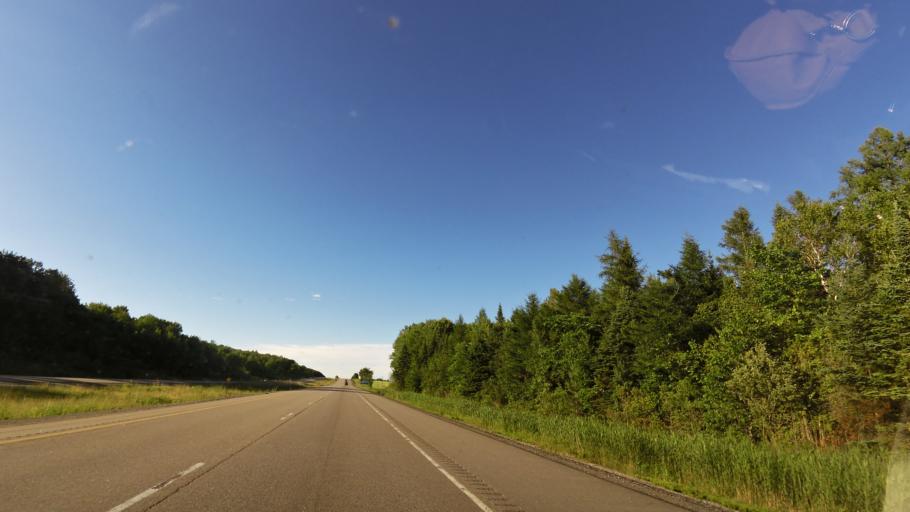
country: CA
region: Ontario
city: Orillia
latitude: 44.6442
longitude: -79.6513
